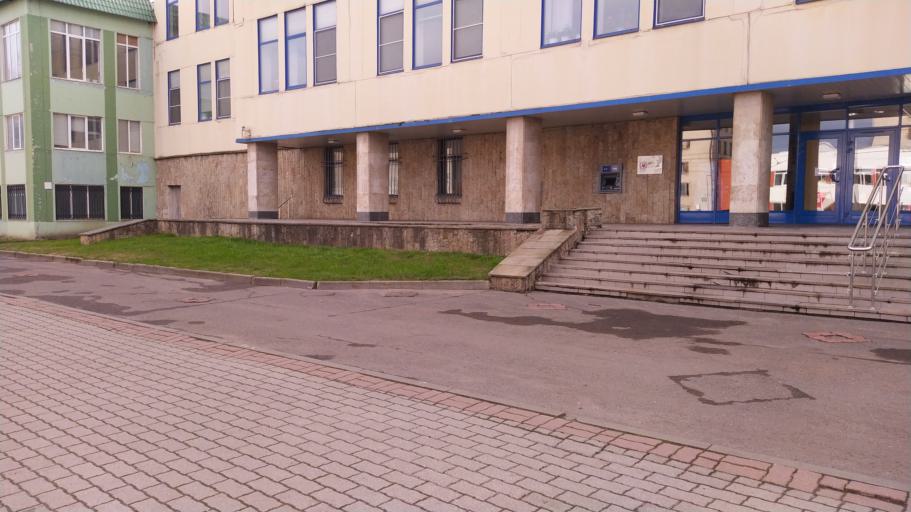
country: RU
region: Jaroslavl
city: Rybinsk
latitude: 58.0562
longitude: 38.7981
